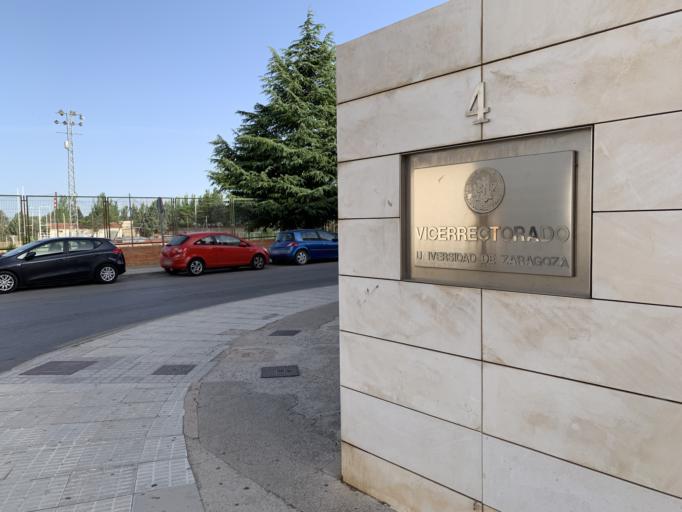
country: ES
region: Aragon
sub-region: Provincia de Teruel
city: Teruel
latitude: 40.3517
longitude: -1.1104
